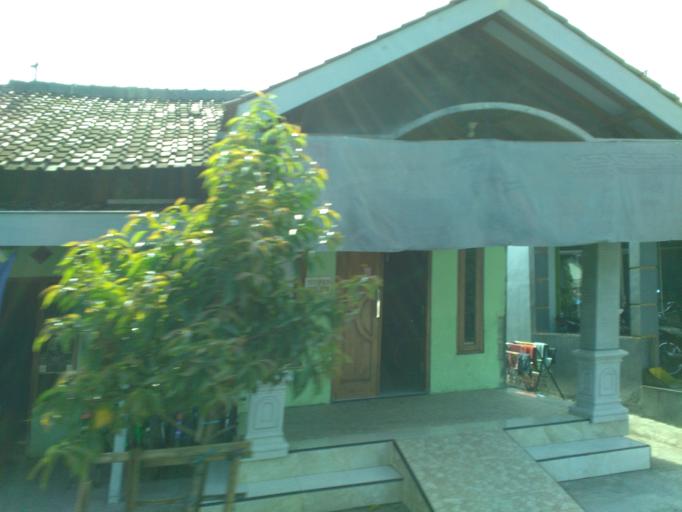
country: ID
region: Central Java
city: Delanggu
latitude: -7.6374
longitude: 110.6917
